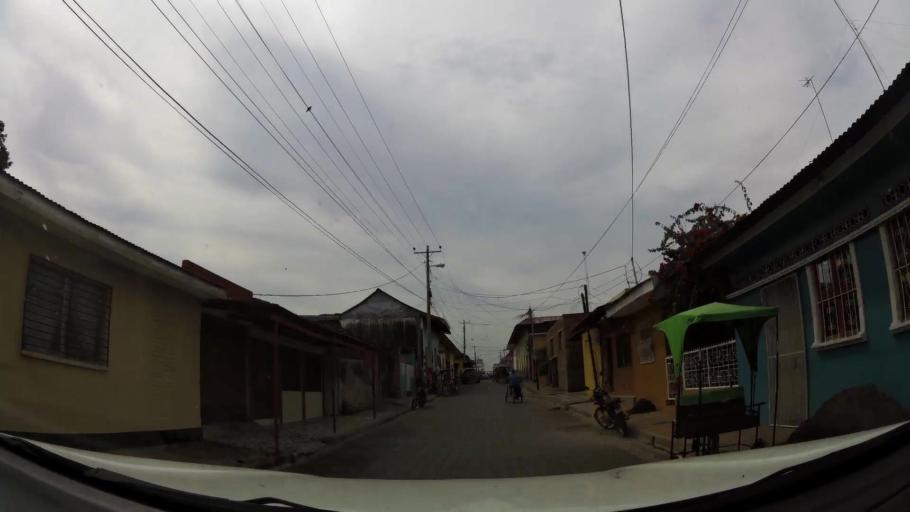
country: NI
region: Rivas
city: Rivas
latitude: 11.4366
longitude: -85.8298
